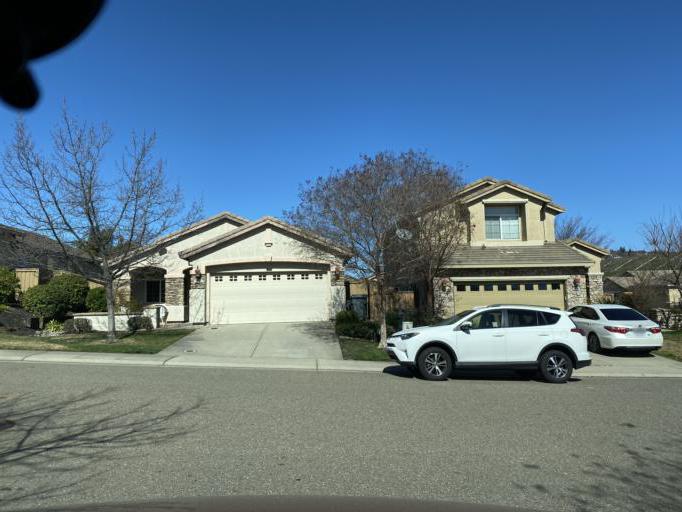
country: US
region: California
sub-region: El Dorado County
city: El Dorado Hills
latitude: 38.6501
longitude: -121.0873
